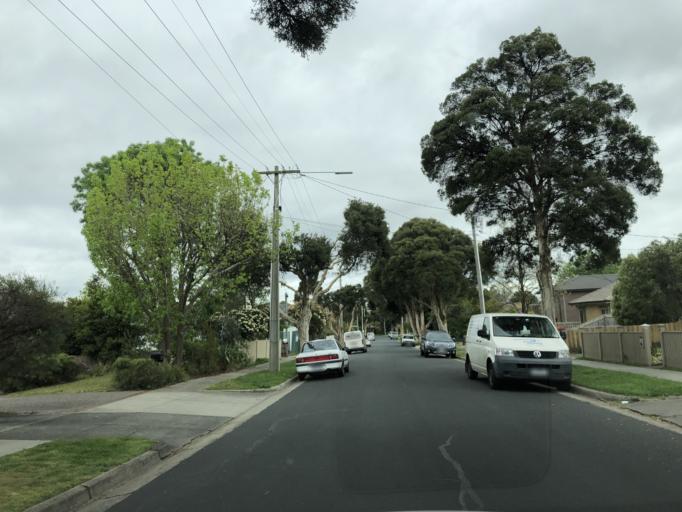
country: AU
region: Victoria
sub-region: Whitehorse
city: Blackburn South
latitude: -37.8368
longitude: 145.1533
